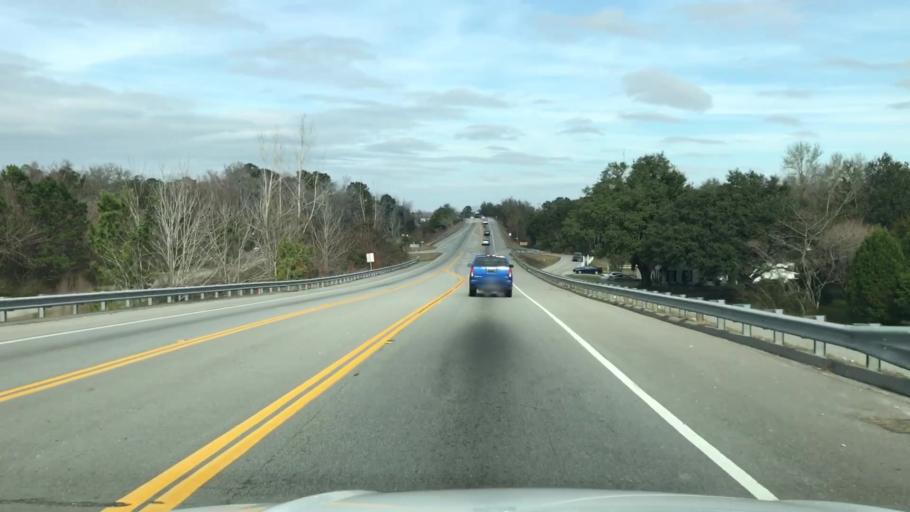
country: US
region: South Carolina
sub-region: Charleston County
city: Shell Point
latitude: 32.7889
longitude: -80.1080
